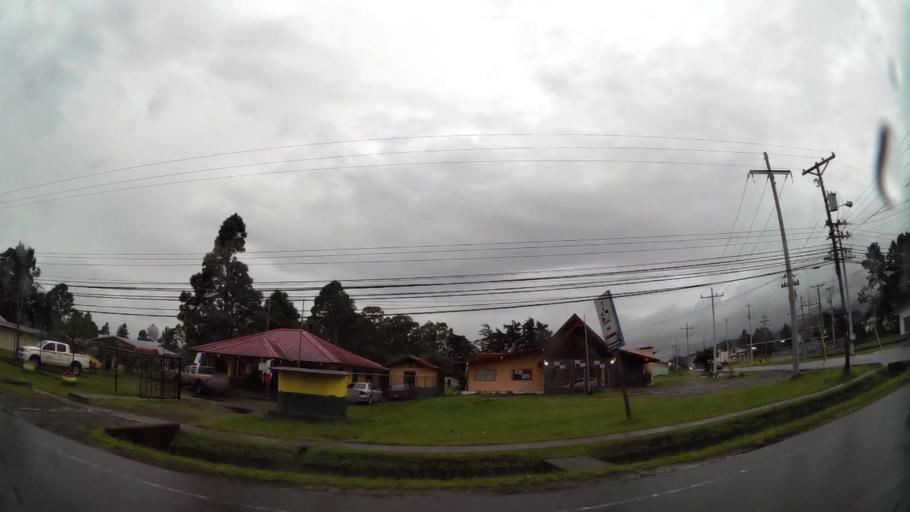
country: PA
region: Chiriqui
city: Volcan
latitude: 8.7788
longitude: -82.6395
